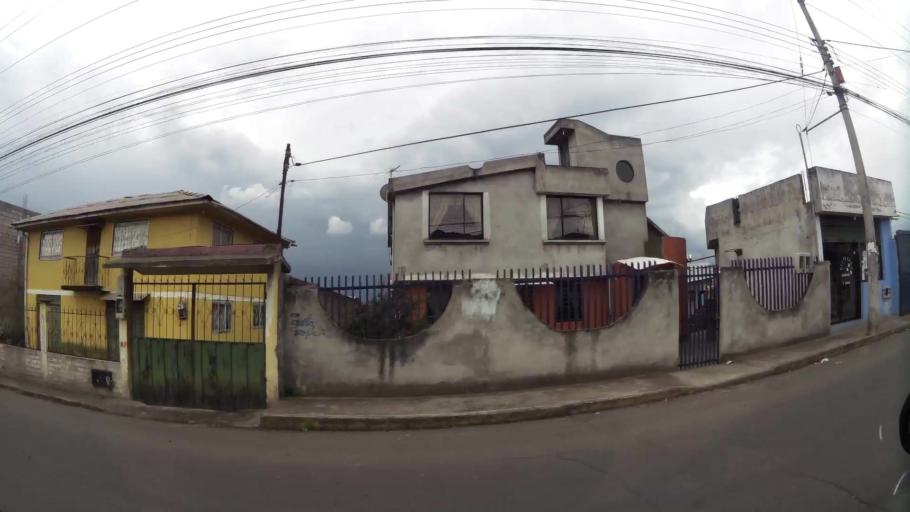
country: EC
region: Pichincha
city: Sangolqui
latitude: -0.3442
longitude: -78.5535
